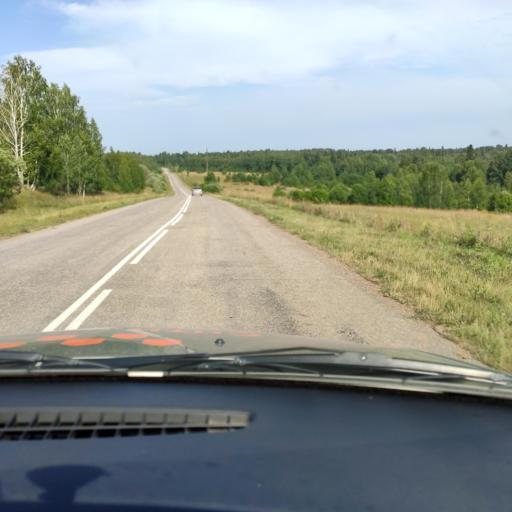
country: RU
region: Bashkortostan
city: Pavlovka
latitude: 55.3981
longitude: 56.5608
